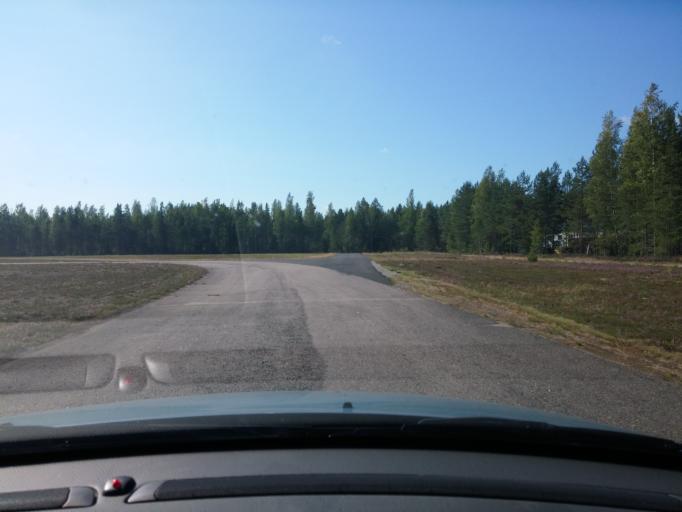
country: FI
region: Uusimaa
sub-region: Helsinki
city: Kaerkoelae
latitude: 60.7415
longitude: 24.0919
